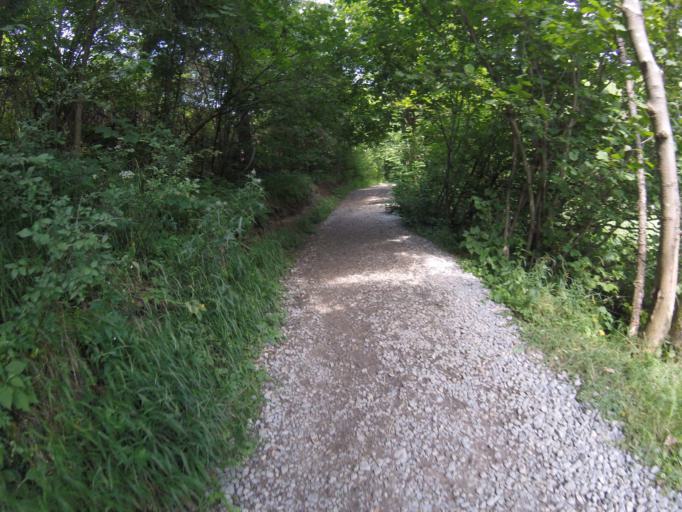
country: SK
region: Zilinsky
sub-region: Okres Zilina
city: Terchova
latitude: 49.2364
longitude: 19.0686
